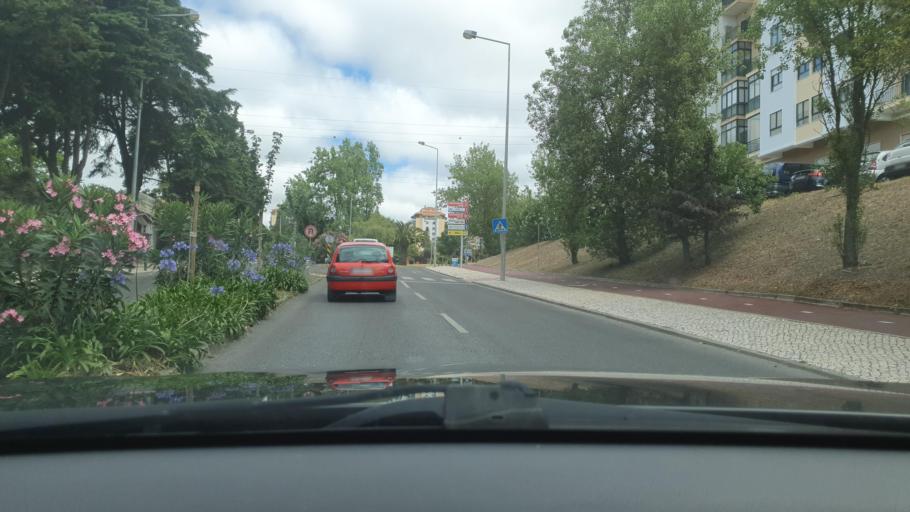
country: PT
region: Lisbon
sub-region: Sintra
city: Cacem
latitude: 38.7605
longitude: -9.2783
